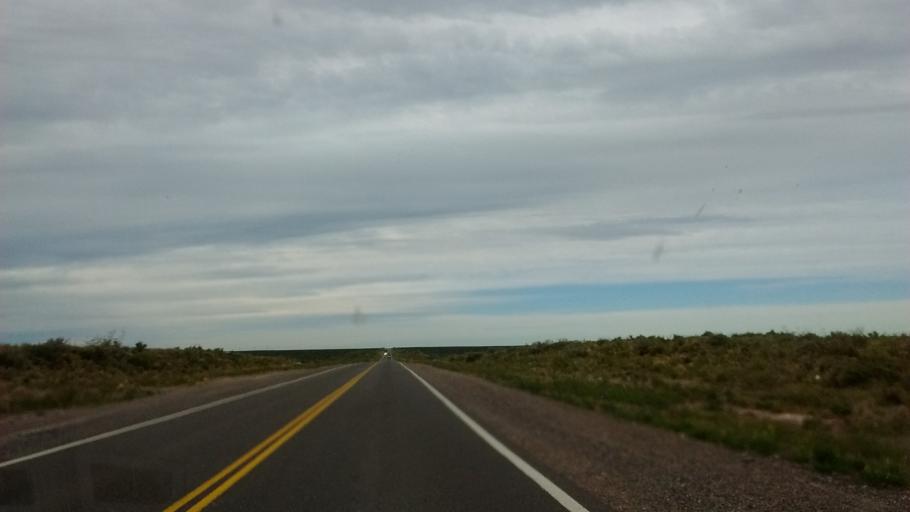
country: AR
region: Rio Negro
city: Catriel
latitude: -38.2620
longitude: -67.9904
